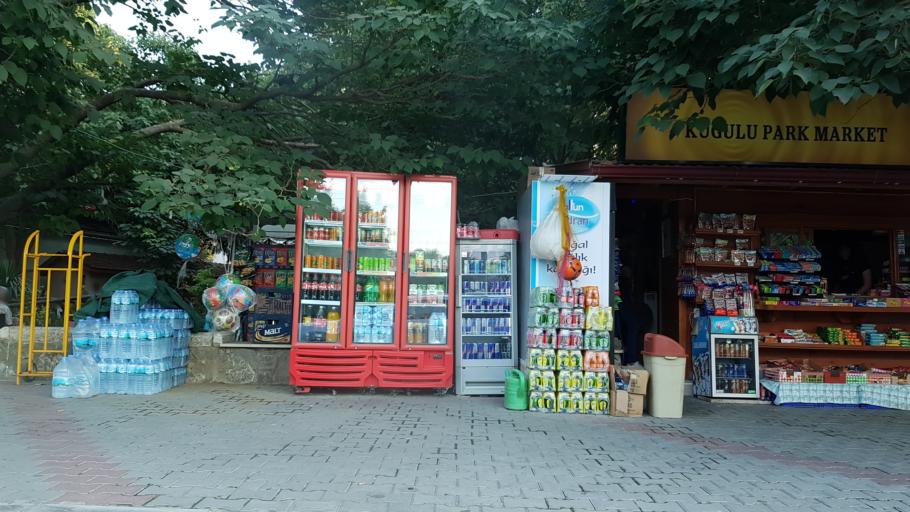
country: TR
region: Izmir
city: Selcuk
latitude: 37.9479
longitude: 27.3668
